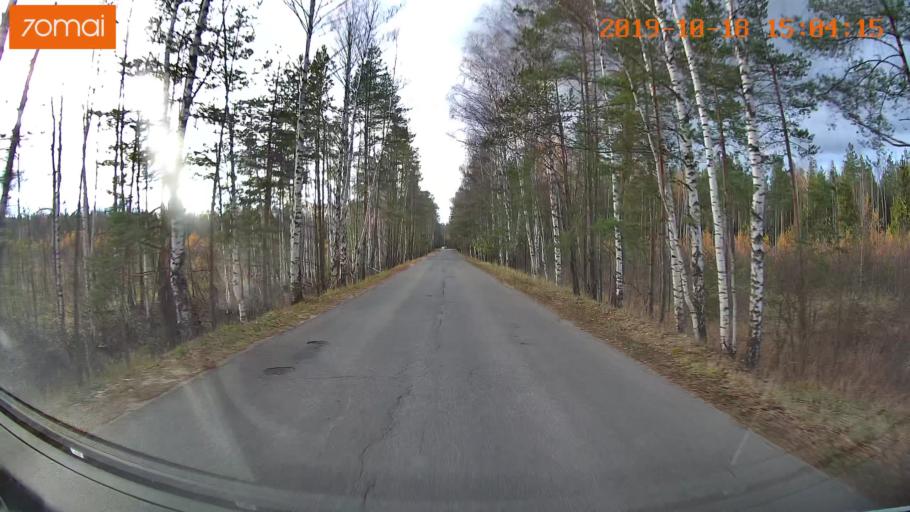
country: RU
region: Vladimir
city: Kurlovo
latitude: 55.5042
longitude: 40.5772
